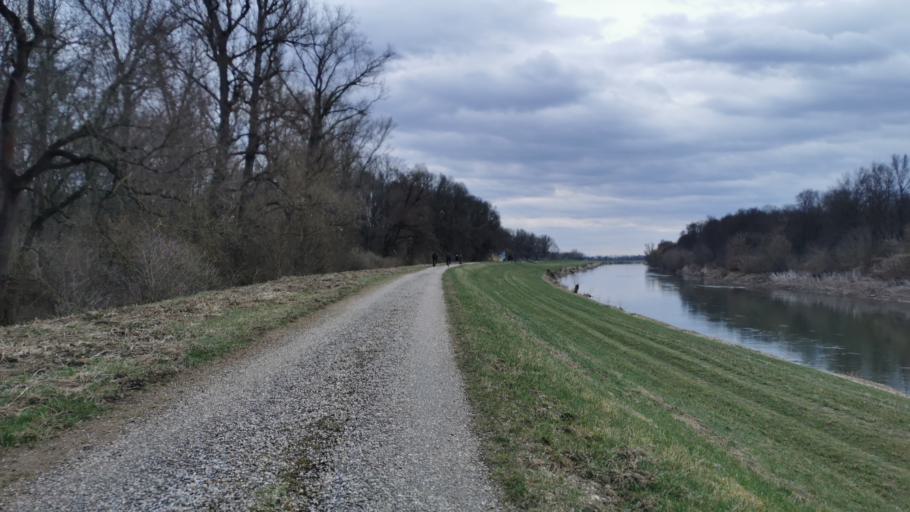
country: CZ
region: South Moravian
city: Hodonin
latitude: 48.8180
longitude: 17.1076
